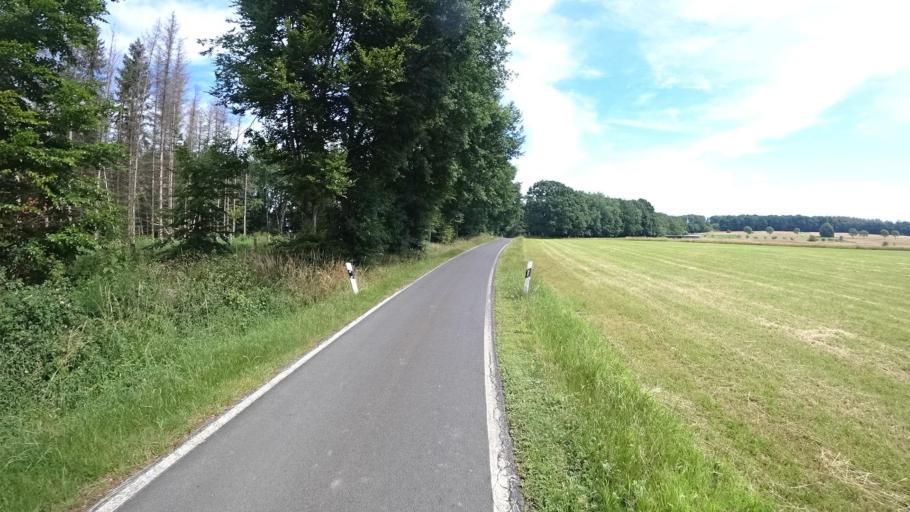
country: DE
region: Rheinland-Pfalz
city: Fluterschen
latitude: 50.6594
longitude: 7.6244
